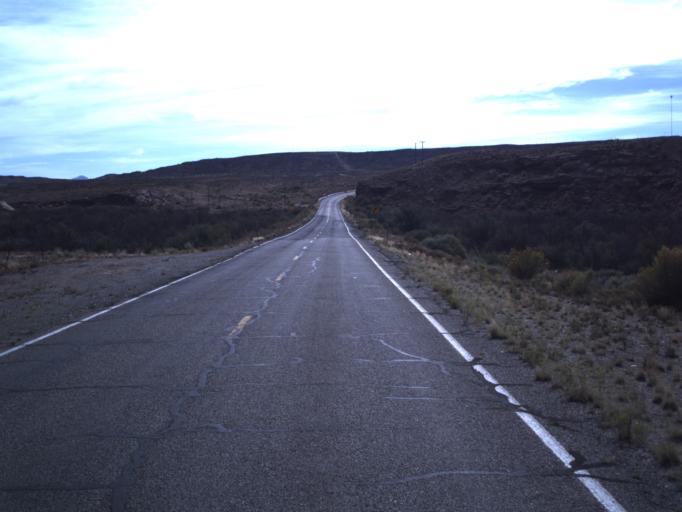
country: US
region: Utah
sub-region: San Juan County
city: Blanding
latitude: 37.3069
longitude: -109.2911
